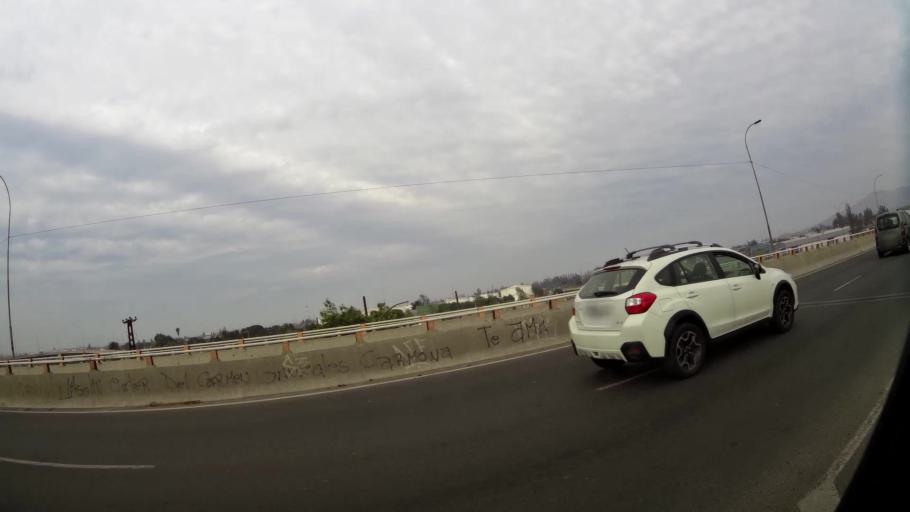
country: CL
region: Santiago Metropolitan
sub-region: Provincia de Maipo
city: San Bernardo
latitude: -33.5275
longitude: -70.7569
